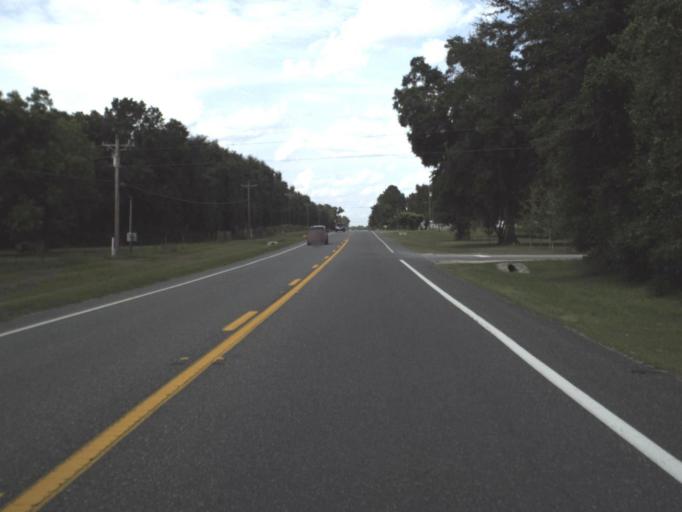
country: US
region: Florida
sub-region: Columbia County
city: Lake City
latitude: 30.0890
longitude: -82.6833
